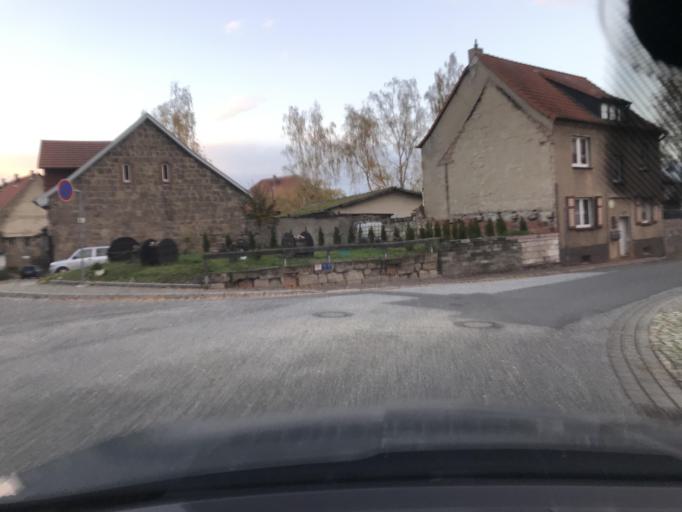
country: DE
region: Saxony-Anhalt
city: Langenstein
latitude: 51.8523
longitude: 10.9870
